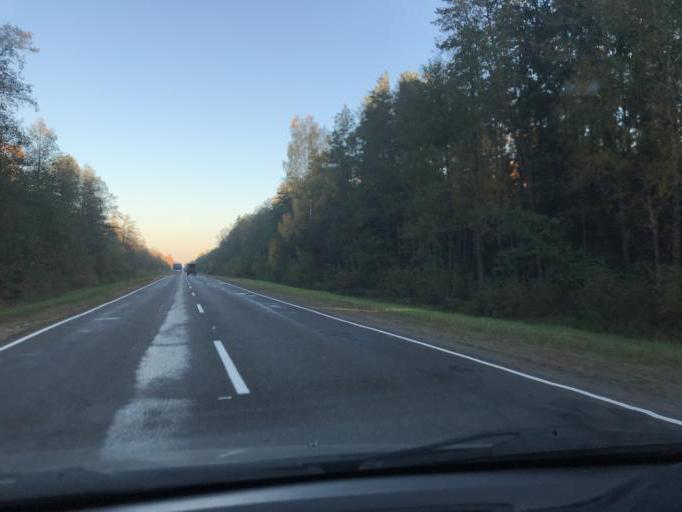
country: BY
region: Minsk
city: Staryya Darohi
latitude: 53.0437
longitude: 28.1367
